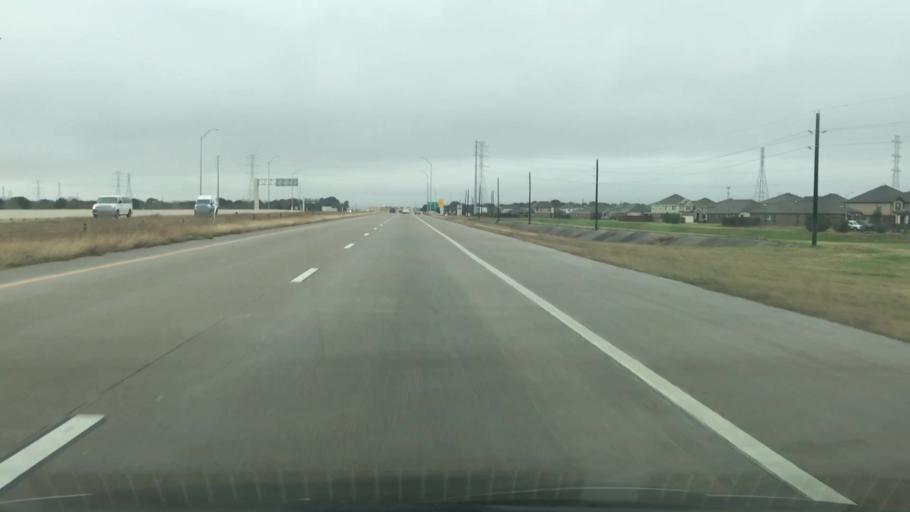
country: US
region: Texas
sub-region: Harris County
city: Katy
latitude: 29.8248
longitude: -95.7654
